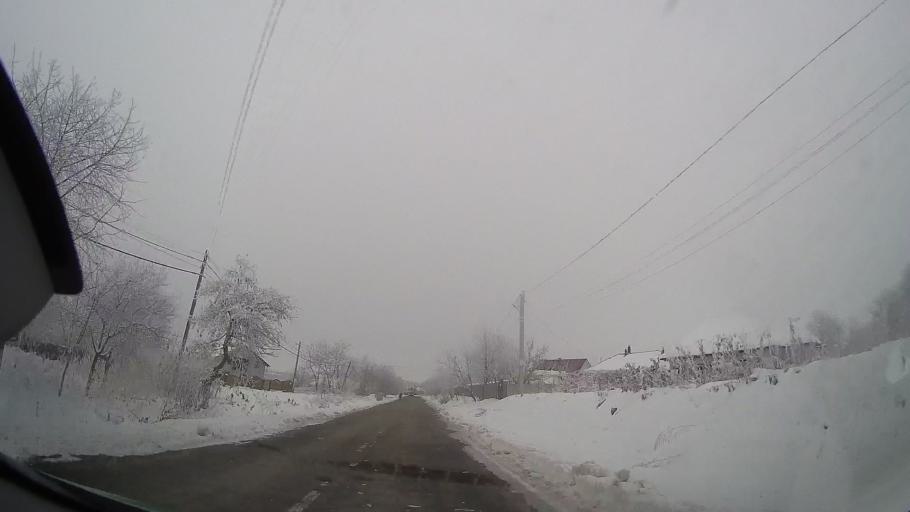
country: RO
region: Neamt
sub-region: Comuna Icusesti
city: Balusesti
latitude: 46.8675
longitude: 26.9949
